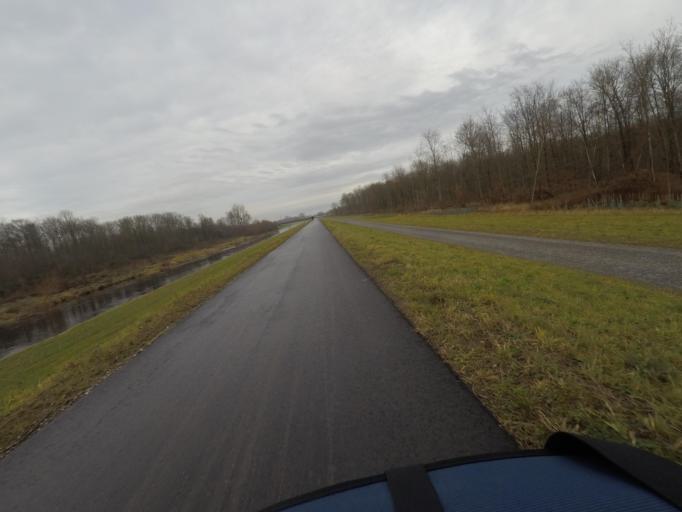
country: DE
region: Baden-Wuerttemberg
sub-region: Karlsruhe Region
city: Rheinau
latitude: 48.8857
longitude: 8.1948
